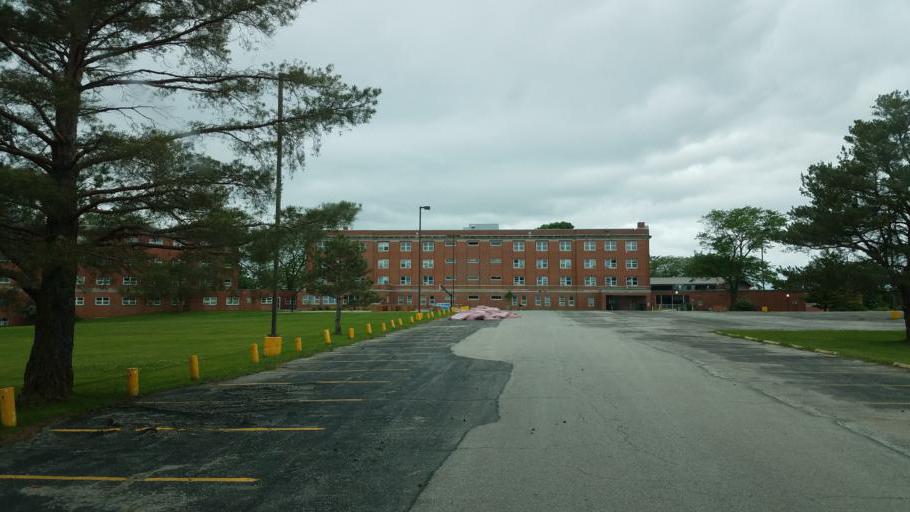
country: US
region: Iowa
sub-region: Decatur County
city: Lamoni
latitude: 40.6175
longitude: -93.9237
